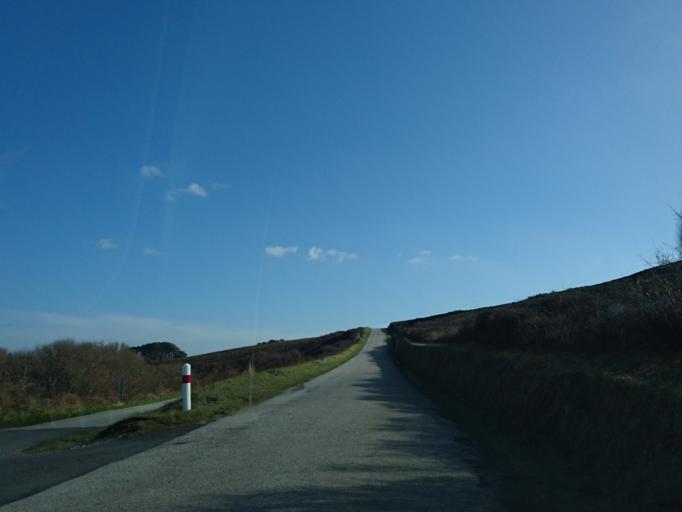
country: FR
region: Brittany
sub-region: Departement du Finistere
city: Roscanvel
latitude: 48.3065
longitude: -4.5701
